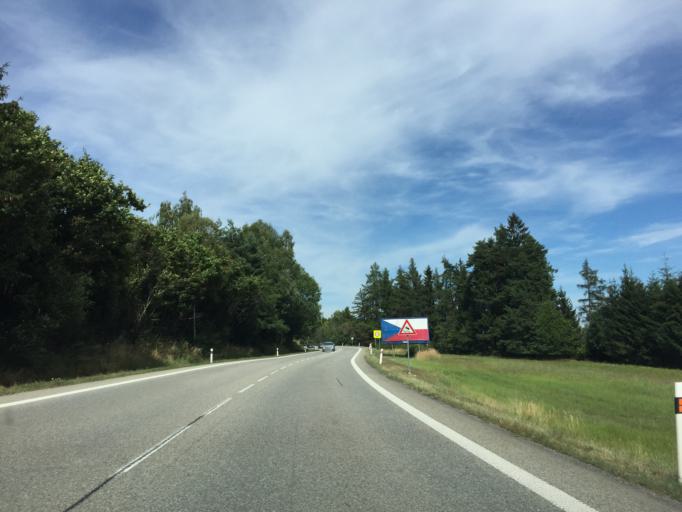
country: CZ
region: Central Bohemia
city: Votice
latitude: 49.5829
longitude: 14.6613
